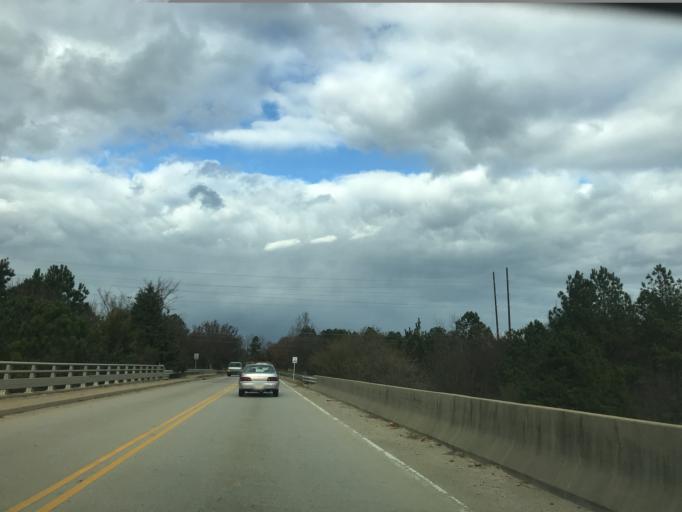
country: US
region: North Carolina
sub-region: Wake County
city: Raleigh
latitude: 35.7832
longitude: -78.5613
